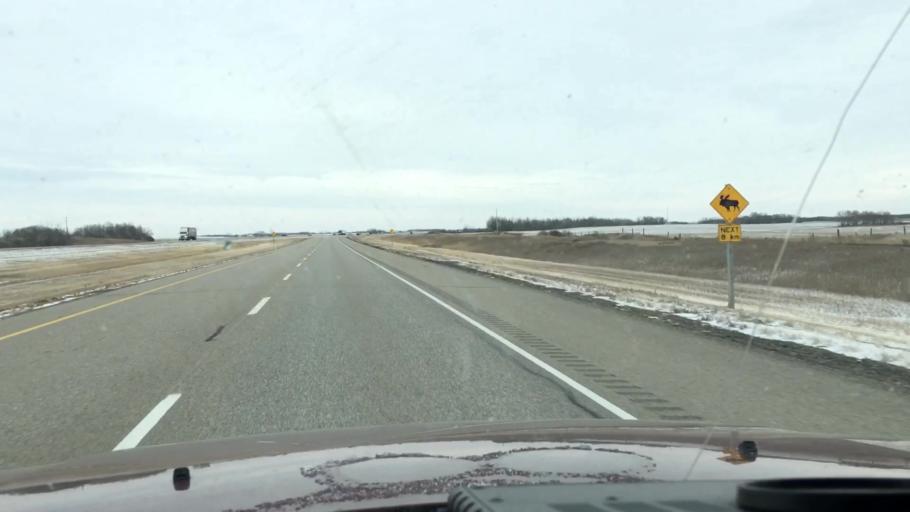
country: CA
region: Saskatchewan
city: Watrous
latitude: 51.3371
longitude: -106.0908
